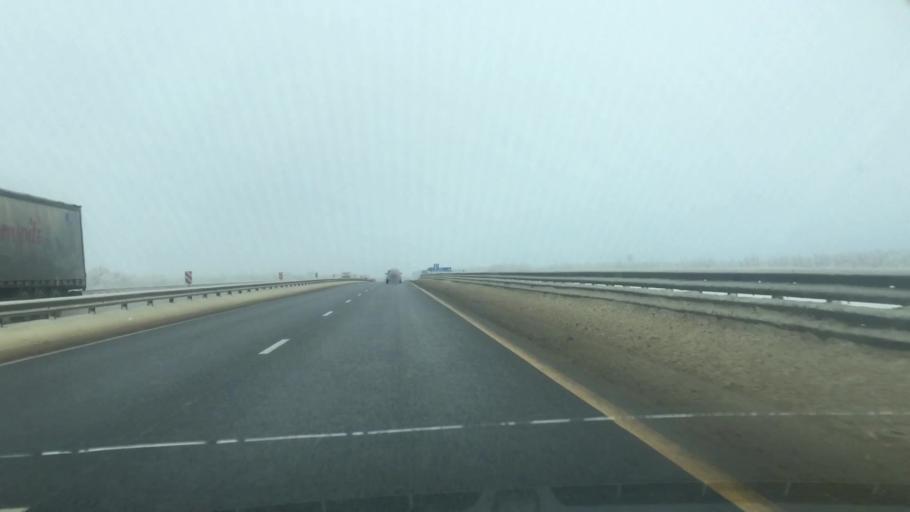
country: RU
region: Lipetsk
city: Zadonsk
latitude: 52.5051
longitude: 38.7555
